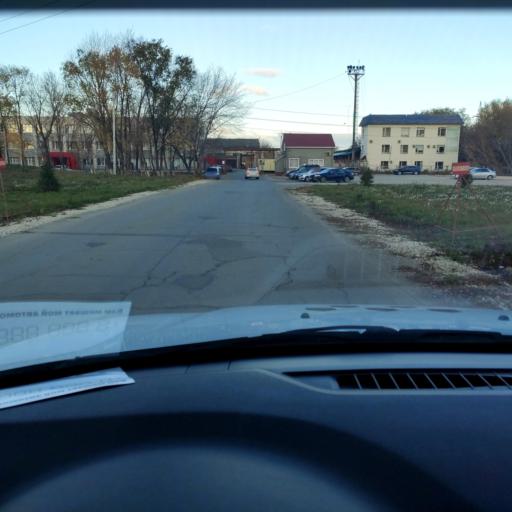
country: RU
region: Samara
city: Tol'yatti
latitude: 53.5140
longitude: 49.4635
